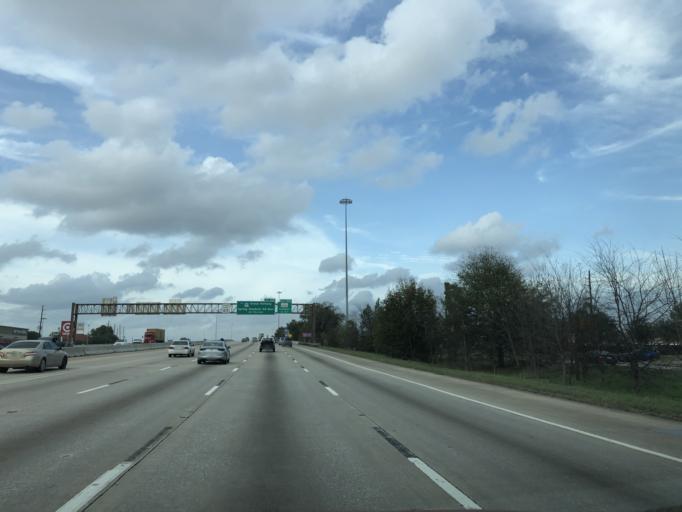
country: US
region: Texas
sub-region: Harris County
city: Spring
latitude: 30.0483
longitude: -95.4307
